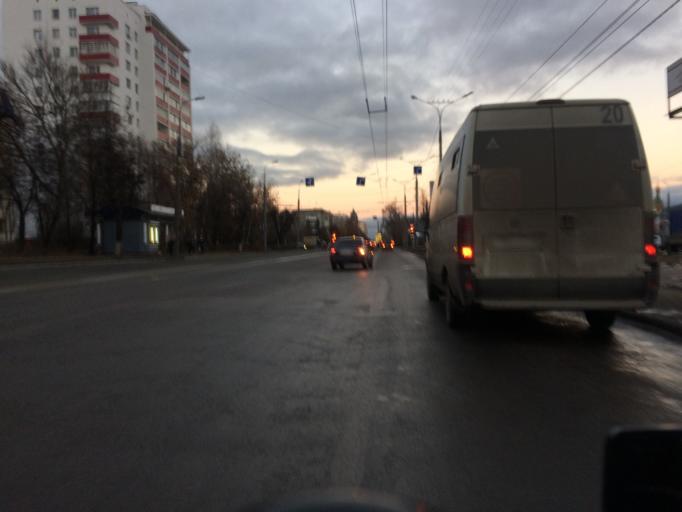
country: RU
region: Mariy-El
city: Yoshkar-Ola
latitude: 56.6280
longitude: 47.8952
